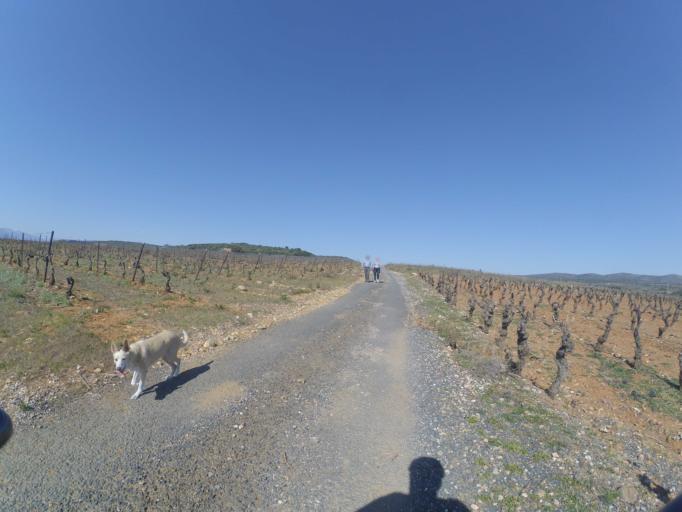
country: FR
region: Languedoc-Roussillon
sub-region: Departement des Pyrenees-Orientales
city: Baixas
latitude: 42.7336
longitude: 2.7810
